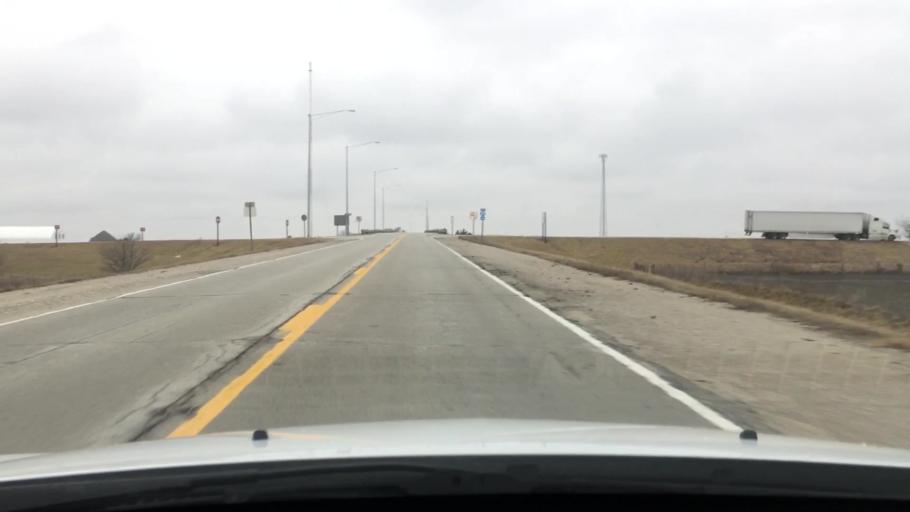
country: US
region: Illinois
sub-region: Iroquois County
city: Clifton
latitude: 40.8842
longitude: -87.9638
